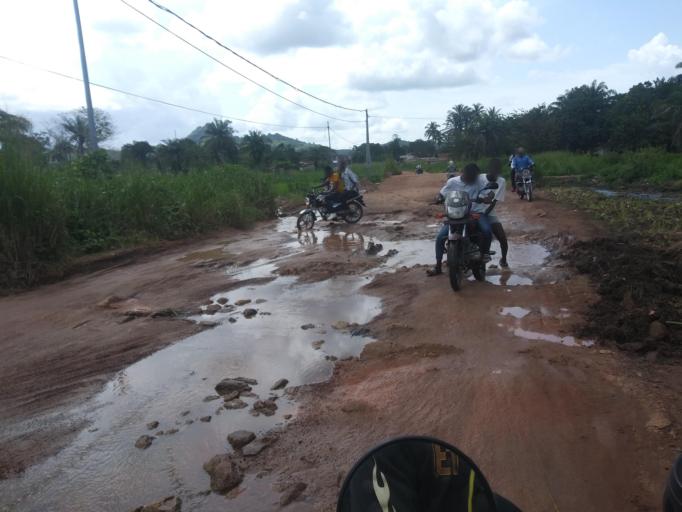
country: SL
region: Northern Province
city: Makeni
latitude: 8.8767
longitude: -12.0415
